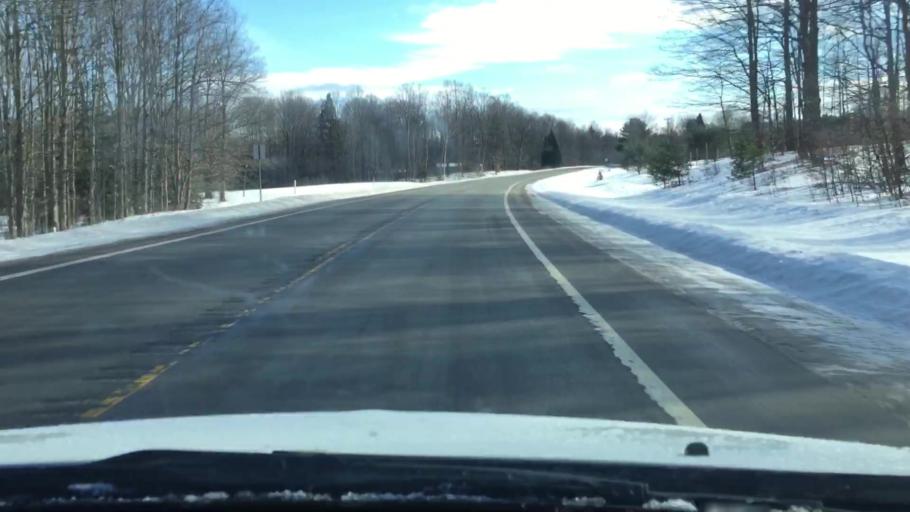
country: US
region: Michigan
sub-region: Antrim County
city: Mancelona
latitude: 44.9863
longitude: -85.0561
